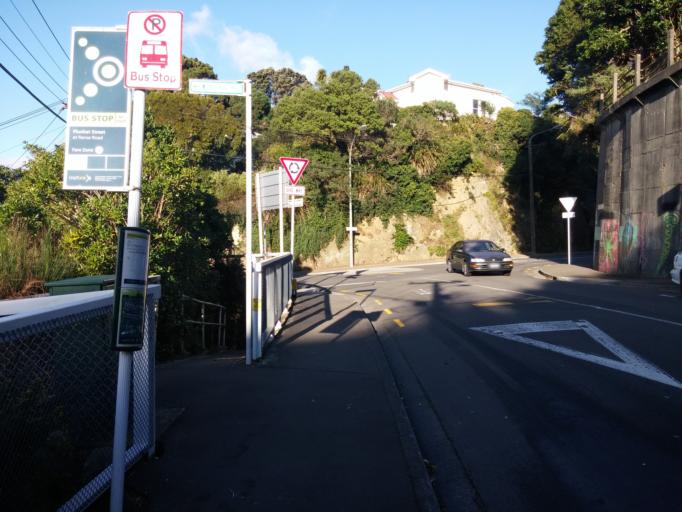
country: NZ
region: Wellington
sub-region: Wellington City
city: Kelburn
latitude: -41.2891
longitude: 174.7585
